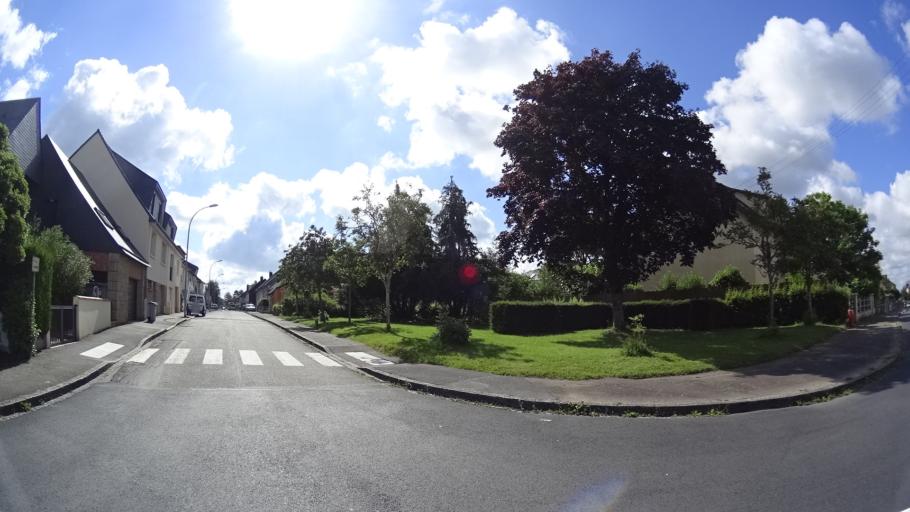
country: FR
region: Brittany
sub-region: Departement d'Ille-et-Vilaine
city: Saint-Gilles
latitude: 48.1284
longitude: -1.8185
